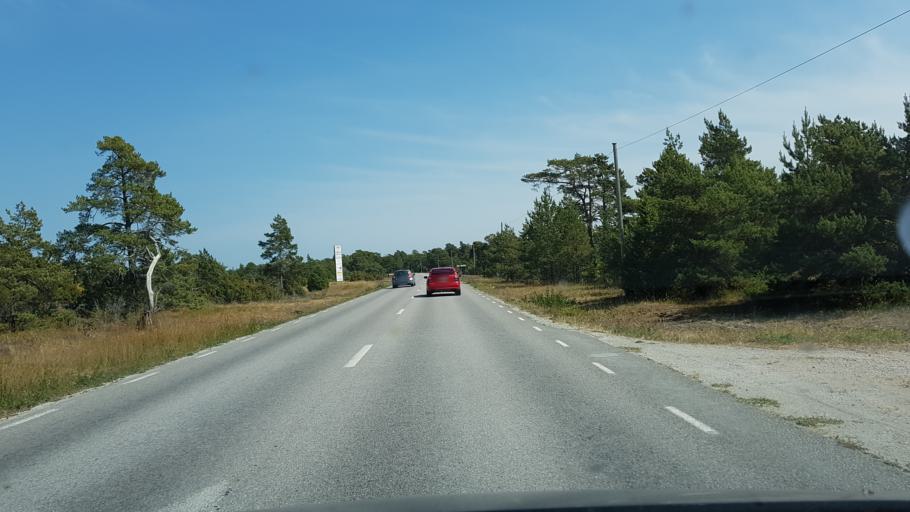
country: SE
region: Gotland
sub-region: Gotland
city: Visby
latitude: 57.6307
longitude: 18.4240
